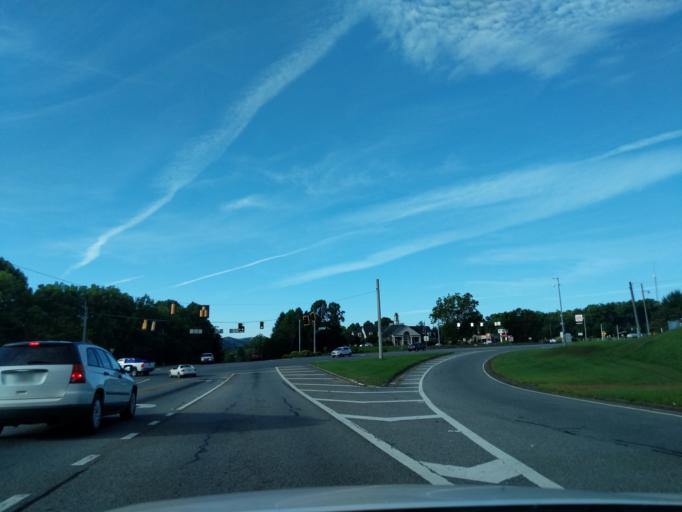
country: US
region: Georgia
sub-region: Fannin County
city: Blue Ridge
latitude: 34.8738
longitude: -84.3226
